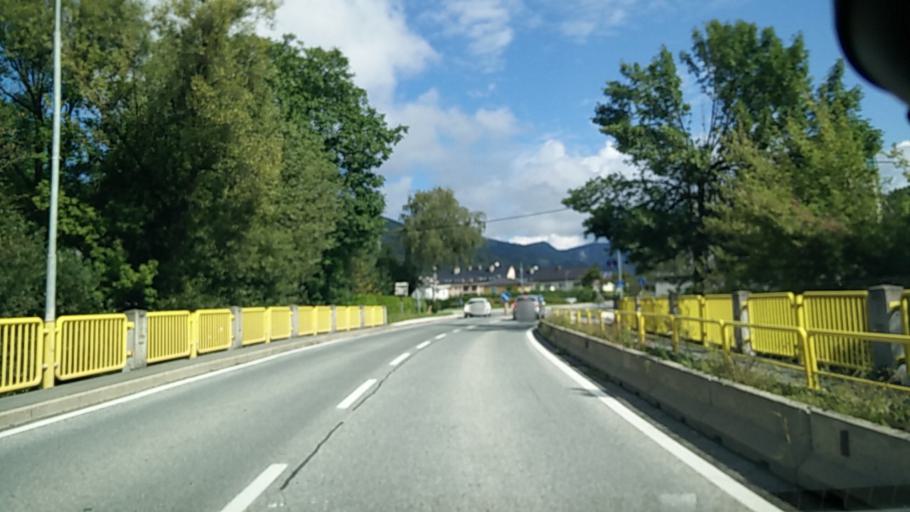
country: AT
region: Carinthia
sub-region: Politischer Bezirk Sankt Veit an der Glan
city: Bruckl
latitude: 46.7475
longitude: 14.5309
